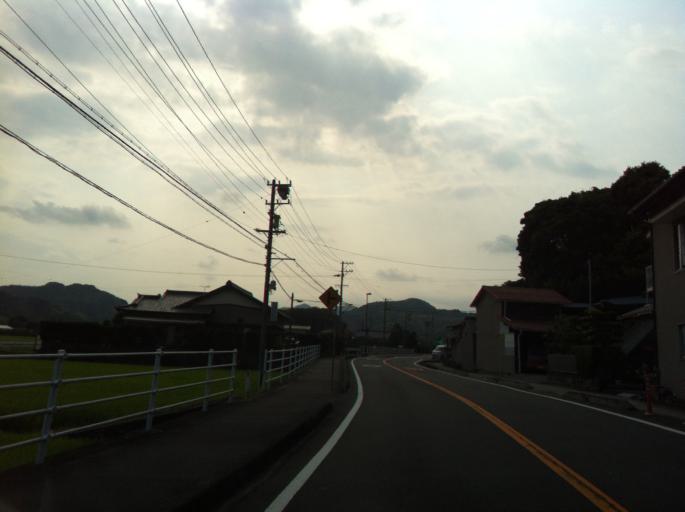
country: JP
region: Shizuoka
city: Fujieda
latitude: 34.9100
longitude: 138.2742
